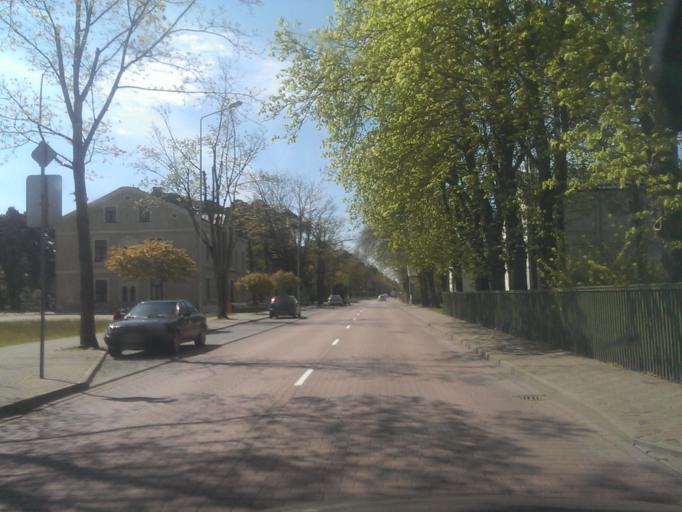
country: LV
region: Ventspils
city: Ventspils
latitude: 57.3916
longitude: 21.5489
